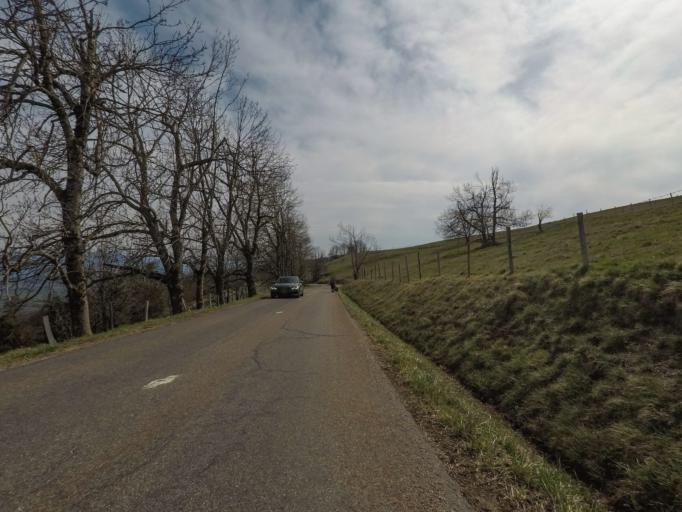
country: FR
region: Rhone-Alpes
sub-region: Departement de la Haute-Savoie
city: Collonges-sous-Saleve
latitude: 46.1318
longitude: 6.1758
